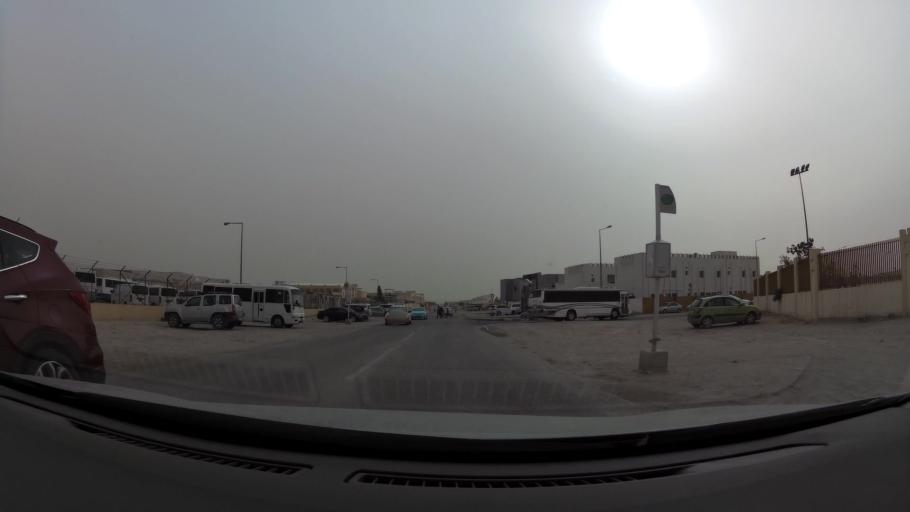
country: QA
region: Baladiyat ad Dawhah
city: Doha
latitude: 25.2389
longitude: 51.5076
